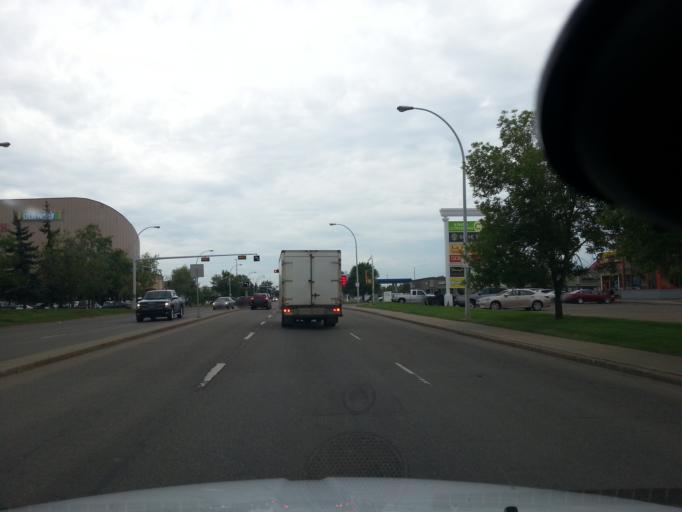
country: CA
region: Alberta
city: St. Albert
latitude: 53.5249
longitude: -113.6165
